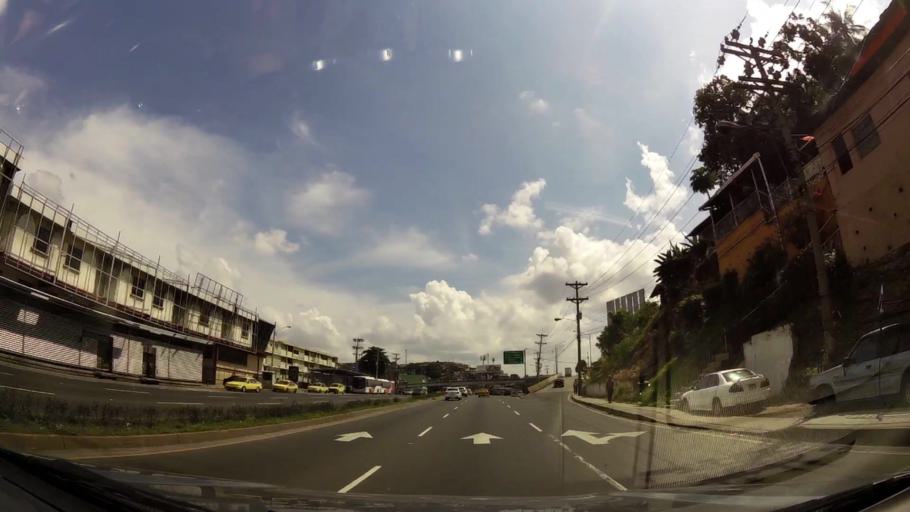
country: PA
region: Panama
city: San Miguelito
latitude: 9.0307
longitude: -79.5018
